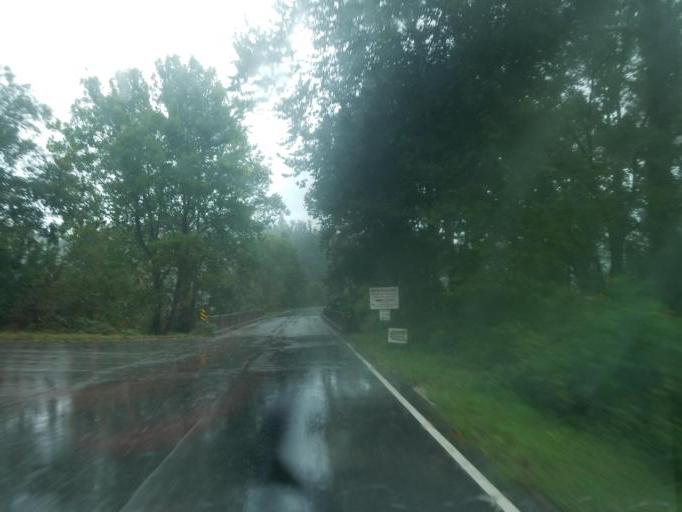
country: US
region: Kentucky
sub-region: Carter County
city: Grayson
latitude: 38.4840
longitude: -83.0316
